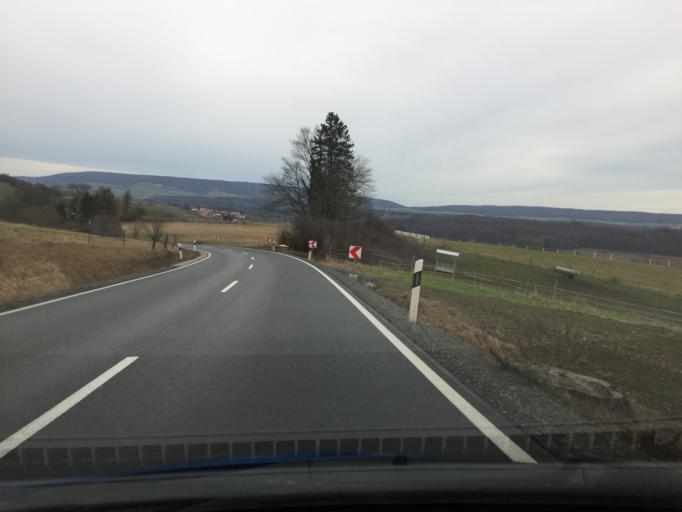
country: DE
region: Lower Saxony
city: Luerdissen
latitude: 51.9732
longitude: 9.6519
